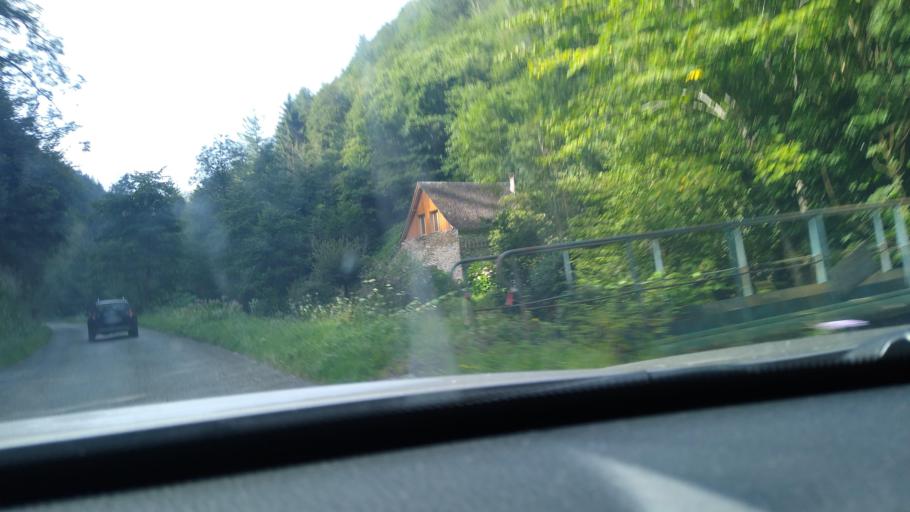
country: FR
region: Midi-Pyrenees
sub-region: Departement de l'Ariege
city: Saint-Girons
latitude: 42.8091
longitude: 1.1964
